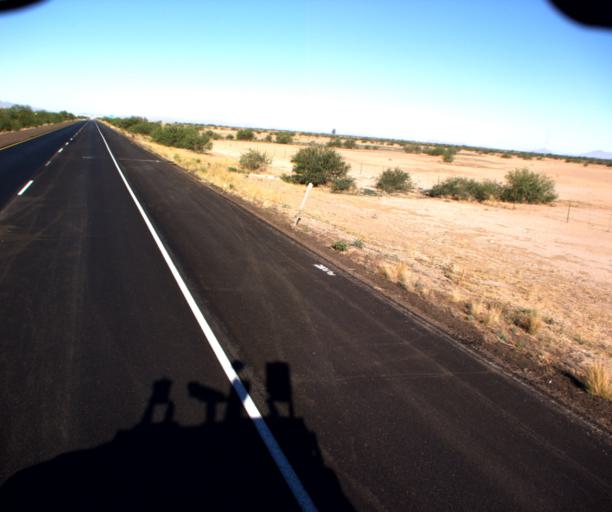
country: US
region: Arizona
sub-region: Pinal County
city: Casa Grande
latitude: 32.8282
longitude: -111.8106
